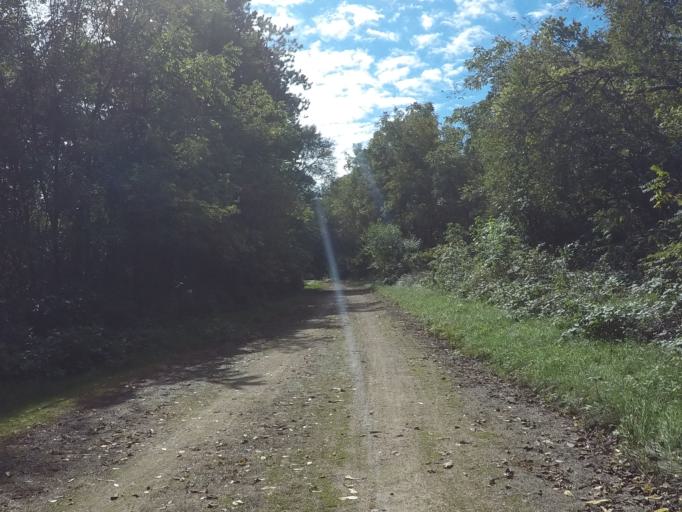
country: US
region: Wisconsin
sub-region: Richland County
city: Richland Center
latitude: 43.2215
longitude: -90.2957
